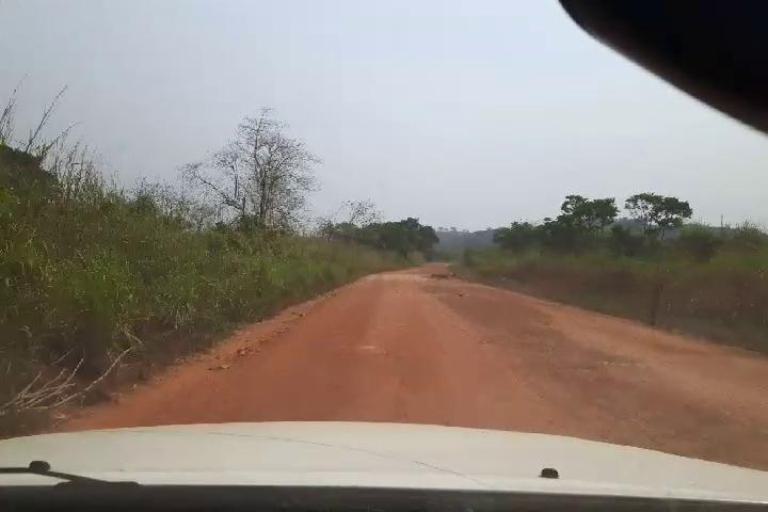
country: SL
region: Northern Province
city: Bumbuna
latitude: 8.9427
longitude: -11.8152
